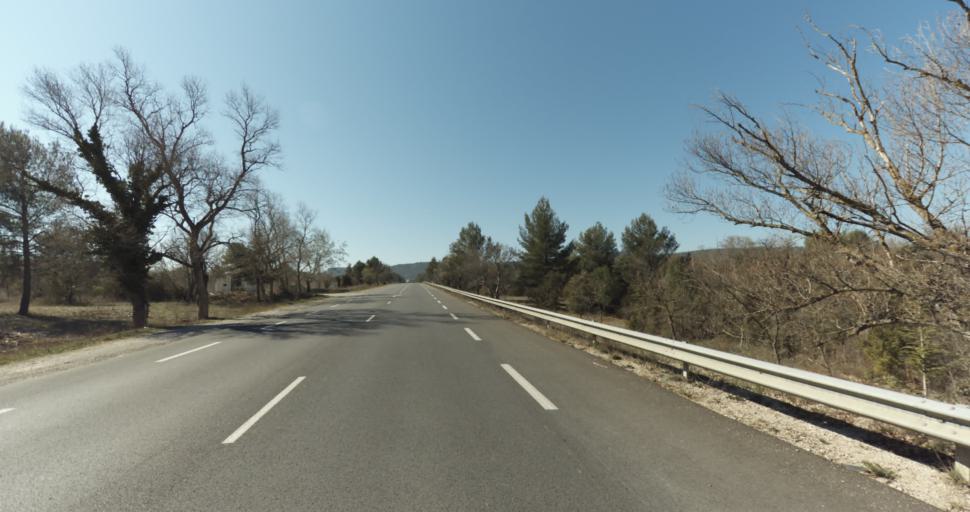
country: FR
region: Provence-Alpes-Cote d'Azur
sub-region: Departement des Bouches-du-Rhone
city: Meyrargues
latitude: 43.6382
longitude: 5.4898
